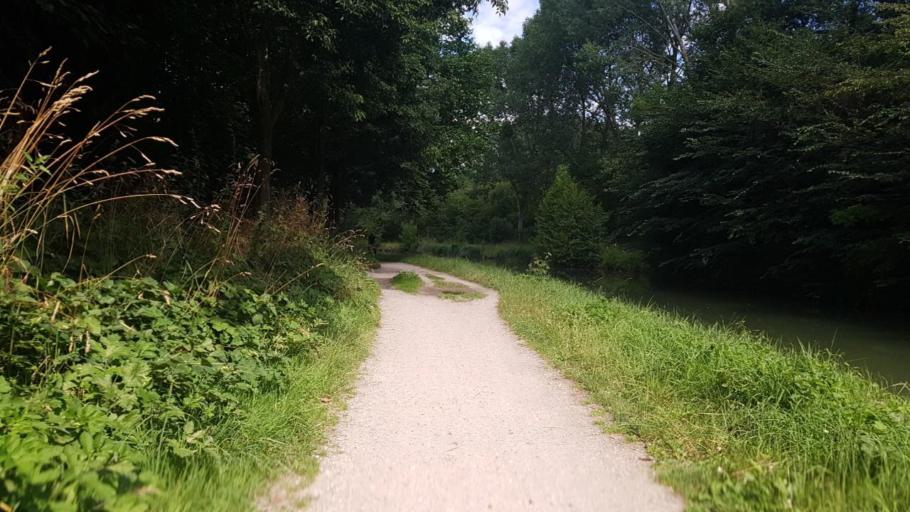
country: FR
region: Ile-de-France
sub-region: Departement de Seine-et-Marne
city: Claye-Souilly
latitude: 48.9585
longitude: 2.6759
